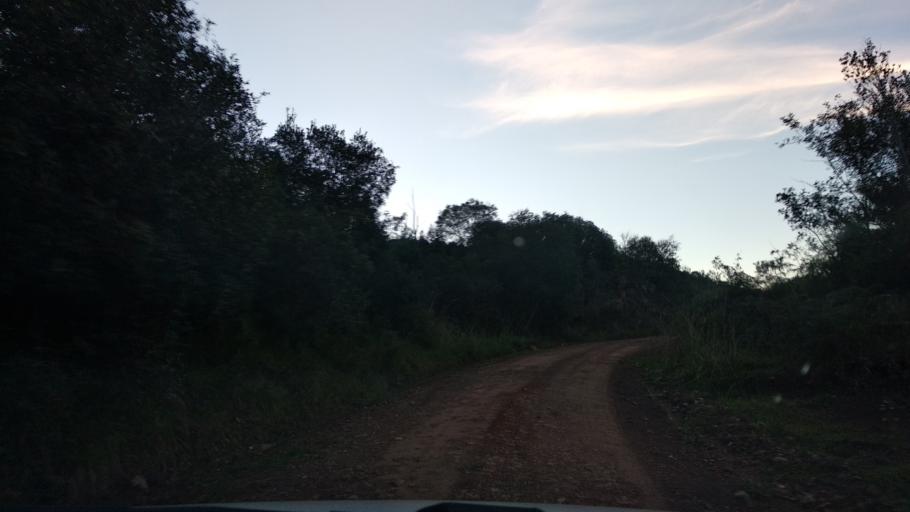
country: BR
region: Santa Catarina
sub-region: Celso Ramos
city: Celso Ramos
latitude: -27.5623
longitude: -51.2367
